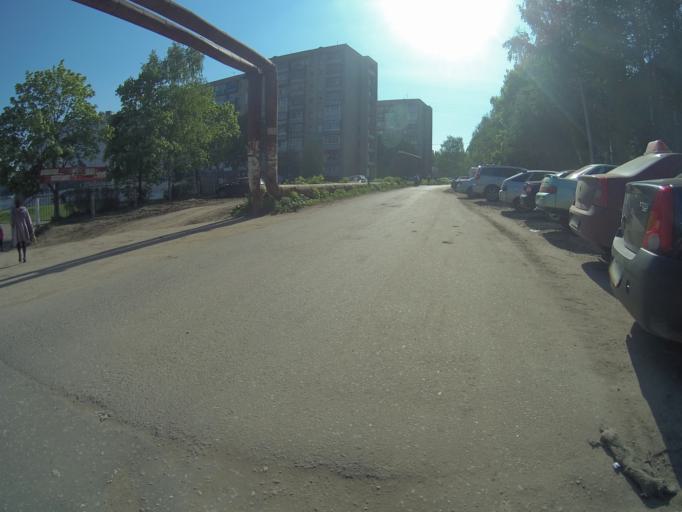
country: RU
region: Vladimir
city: Bogolyubovo
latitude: 56.1716
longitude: 40.4778
